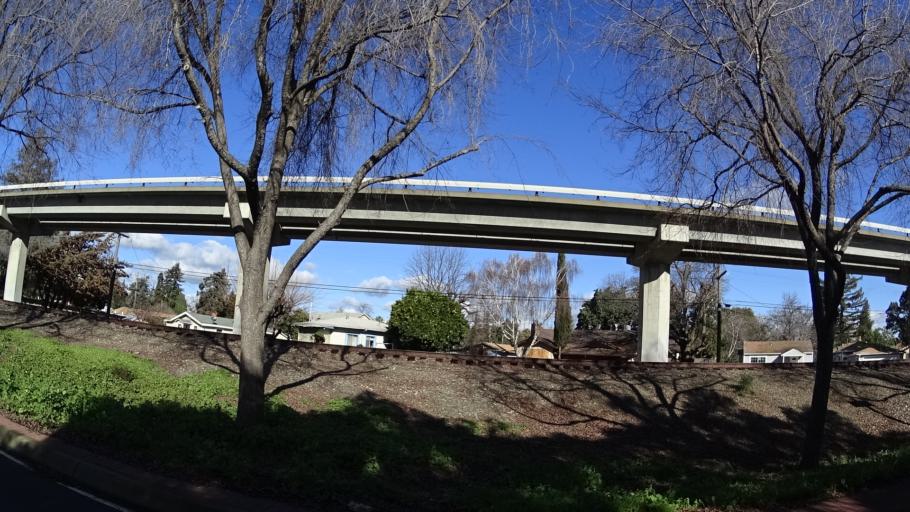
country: US
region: California
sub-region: Alameda County
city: Cherryland
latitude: 37.6827
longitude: -122.1065
